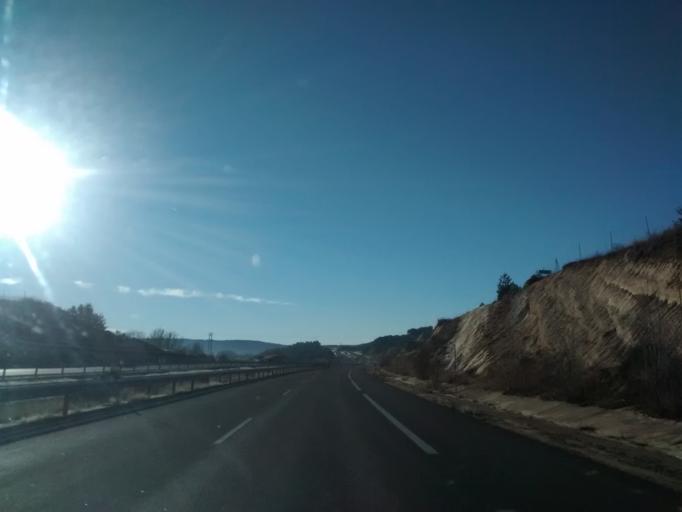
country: ES
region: Castille and Leon
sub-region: Provincia de Palencia
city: Aguilar de Campoo
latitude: 42.7410
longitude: -4.2900
